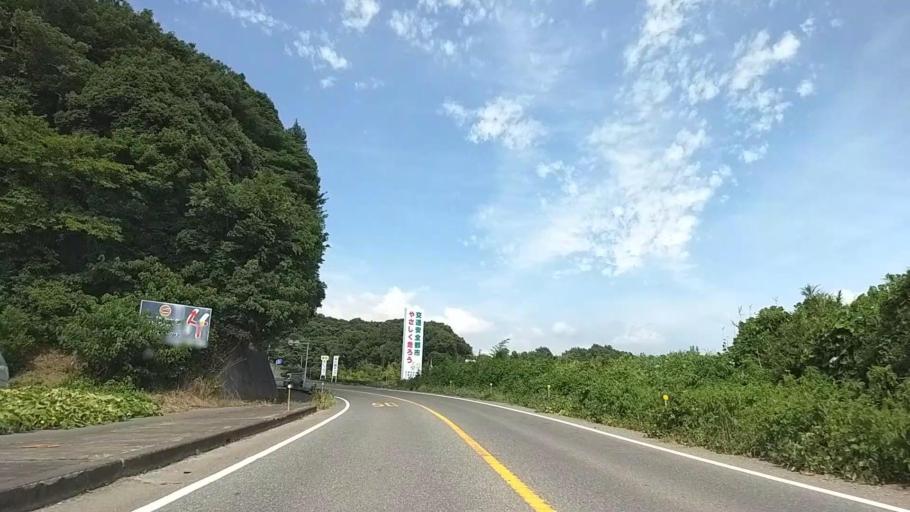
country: JP
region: Shizuoka
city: Mishima
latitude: 35.1343
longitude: 138.9509
